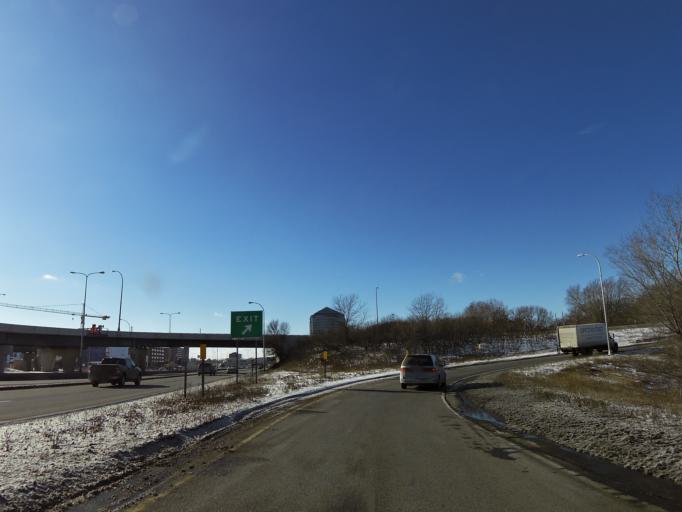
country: US
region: Minnesota
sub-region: Hennepin County
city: Saint Louis Park
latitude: 44.9711
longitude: -93.3417
